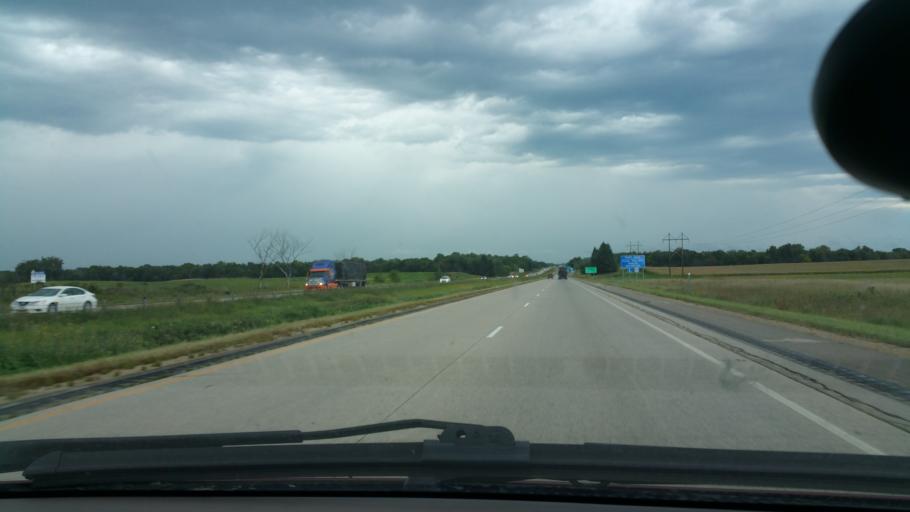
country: US
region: Minnesota
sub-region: Rice County
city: Dundas
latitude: 44.4404
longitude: -93.2923
